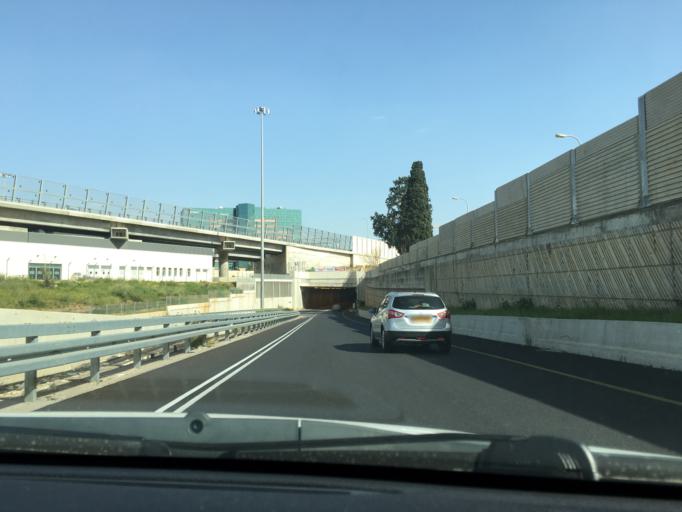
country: IL
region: Central District
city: Hod HaSharon
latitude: 32.1716
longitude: 34.8855
